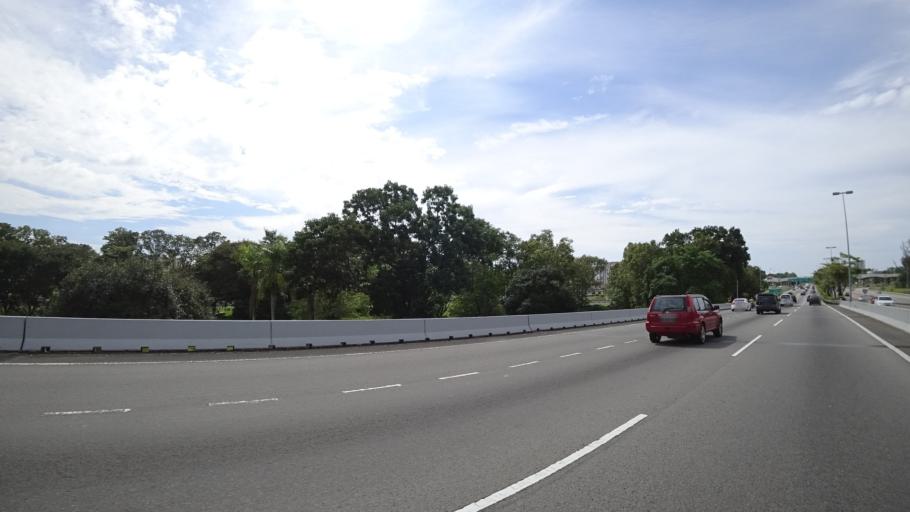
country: BN
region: Brunei and Muara
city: Bandar Seri Begawan
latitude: 4.9107
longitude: 114.9210
